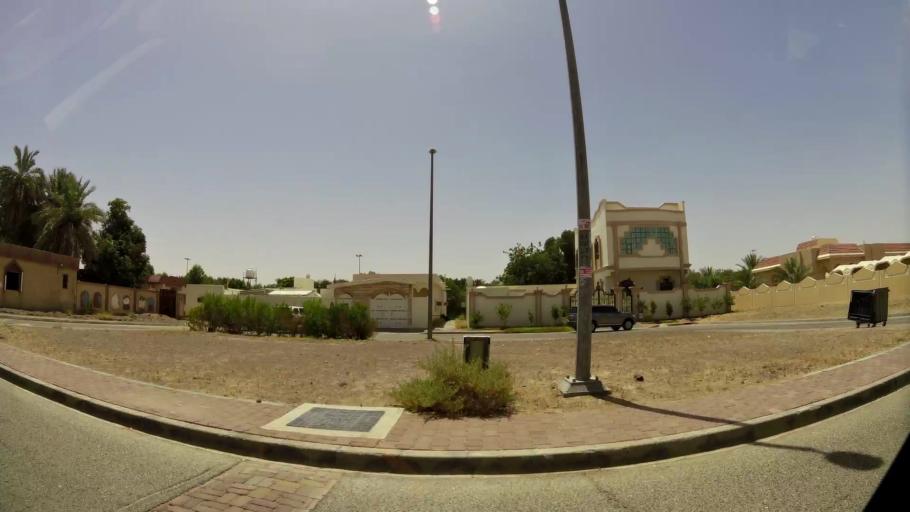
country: OM
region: Al Buraimi
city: Al Buraymi
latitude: 24.2795
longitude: 55.7627
